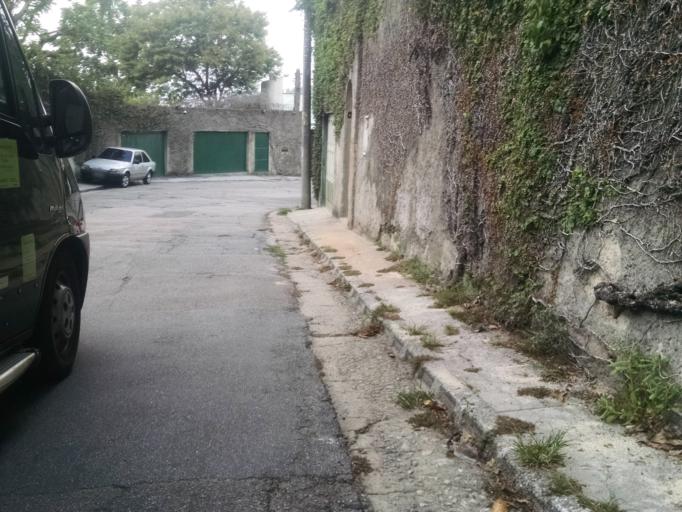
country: BR
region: Rio de Janeiro
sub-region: Rio De Janeiro
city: Rio de Janeiro
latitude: -22.9357
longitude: -43.1963
